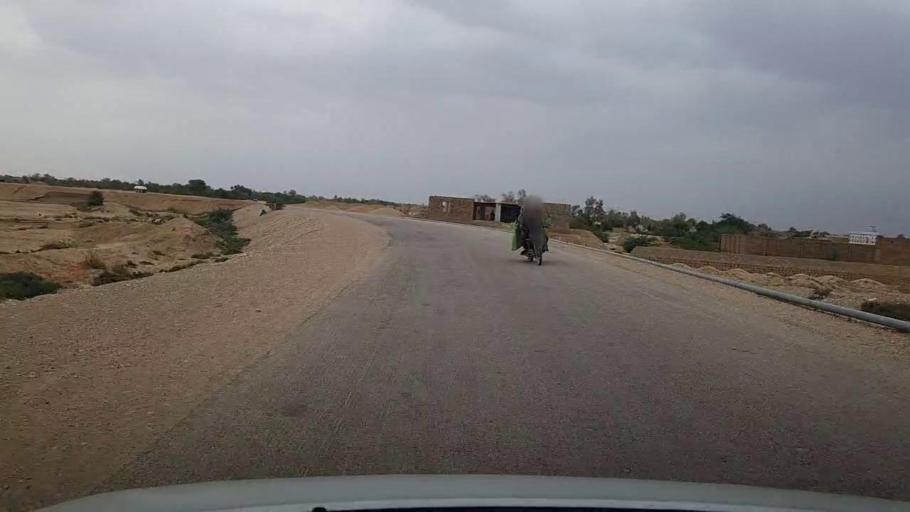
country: PK
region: Sindh
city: Sehwan
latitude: 26.3403
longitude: 67.7264
